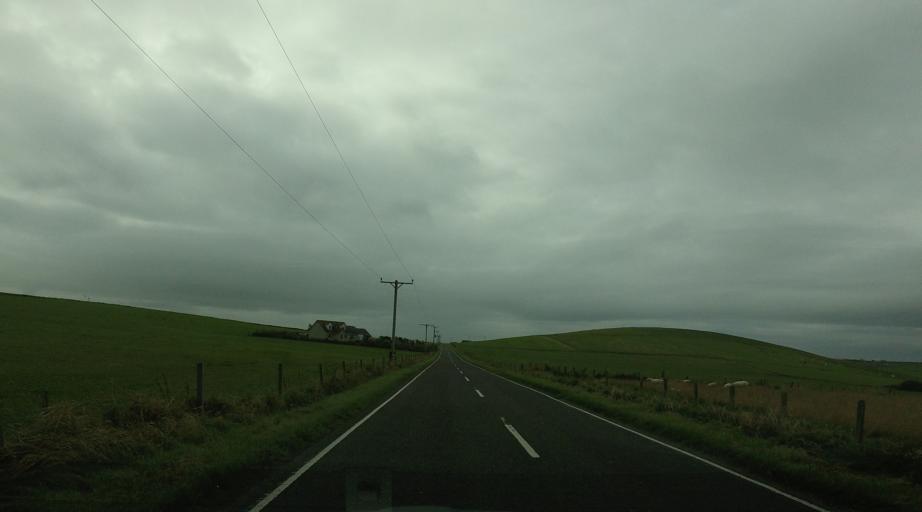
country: GB
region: Scotland
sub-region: Orkney Islands
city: Orkney
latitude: 58.8007
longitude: -2.9615
